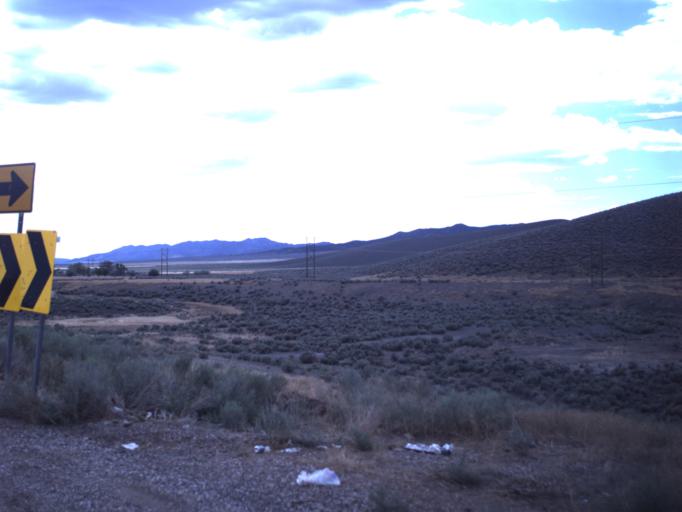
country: US
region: Utah
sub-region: Beaver County
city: Beaver
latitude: 38.0725
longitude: -112.6904
